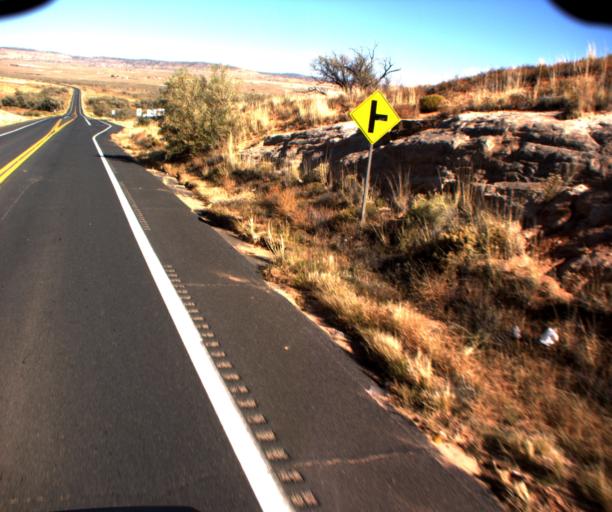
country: US
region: Arizona
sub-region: Coconino County
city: Kaibito
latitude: 36.3211
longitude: -110.9420
